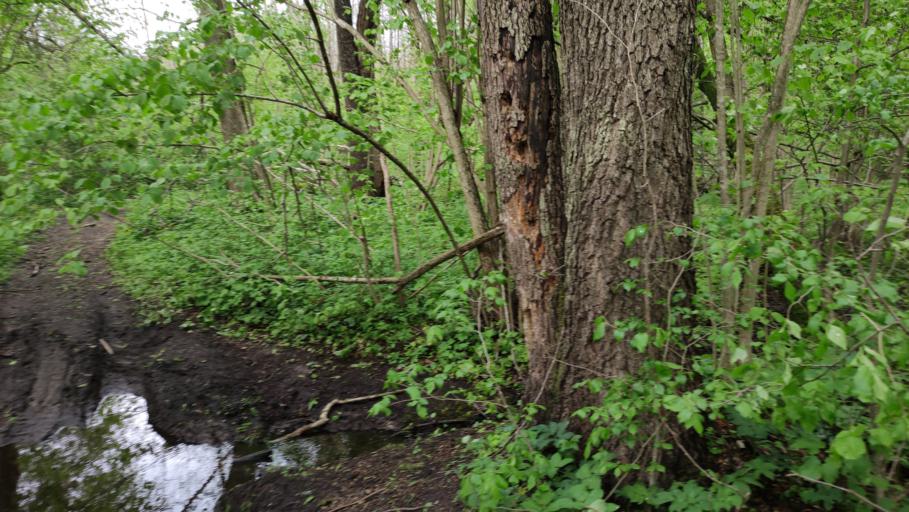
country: LT
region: Alytaus apskritis
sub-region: Alytus
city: Alytus
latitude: 54.4410
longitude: 24.0747
